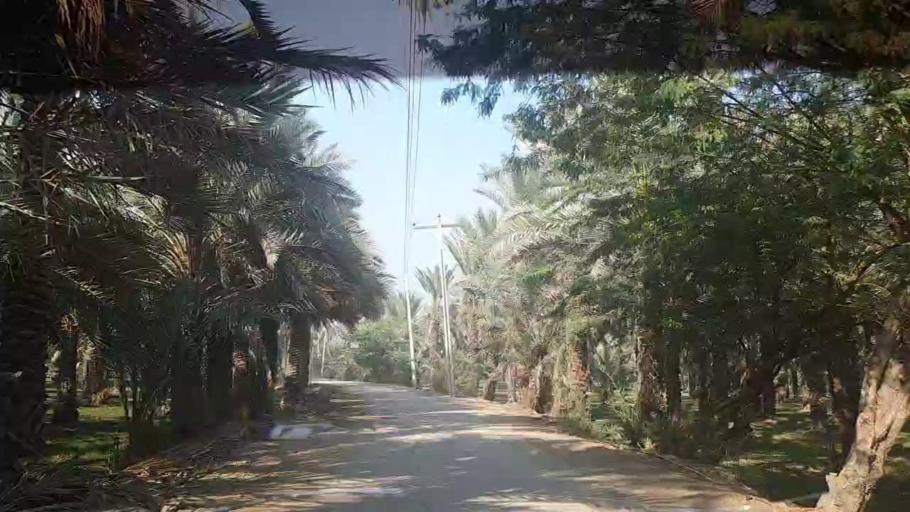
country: PK
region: Sindh
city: Khairpur
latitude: 27.4674
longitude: 68.7159
